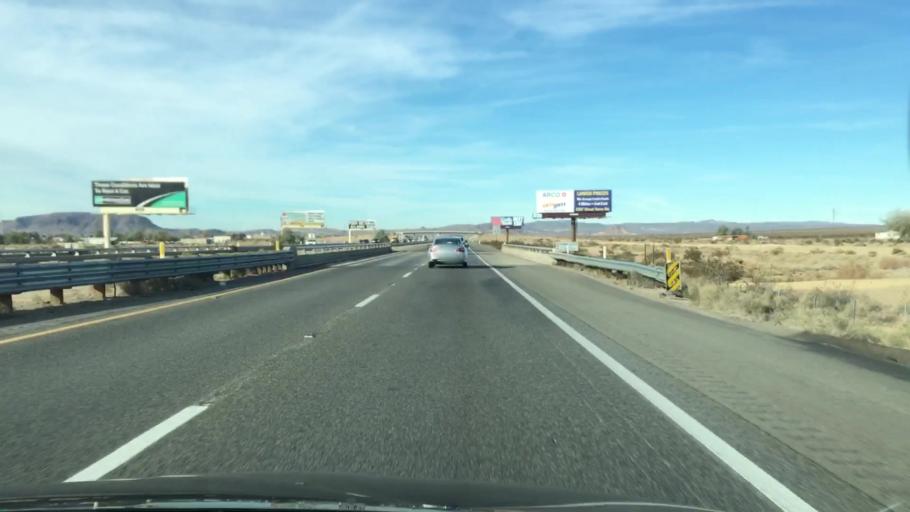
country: US
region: California
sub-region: San Bernardino County
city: Barstow
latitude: 34.9110
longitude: -116.8131
